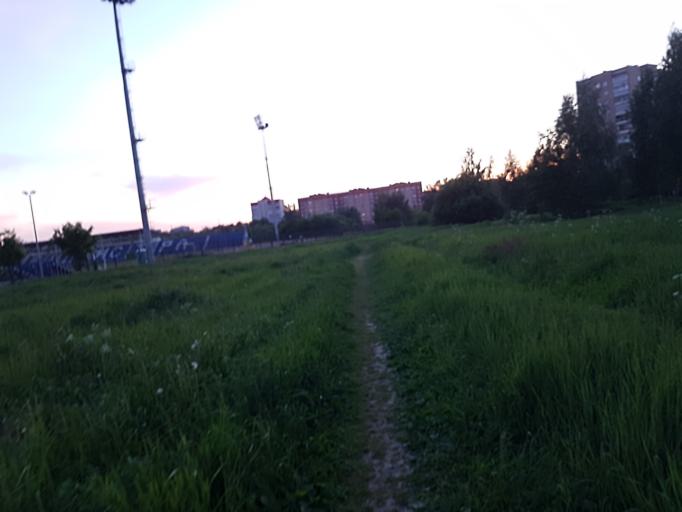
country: RU
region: Moskovskaya
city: Istra
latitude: 55.9069
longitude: 36.8758
